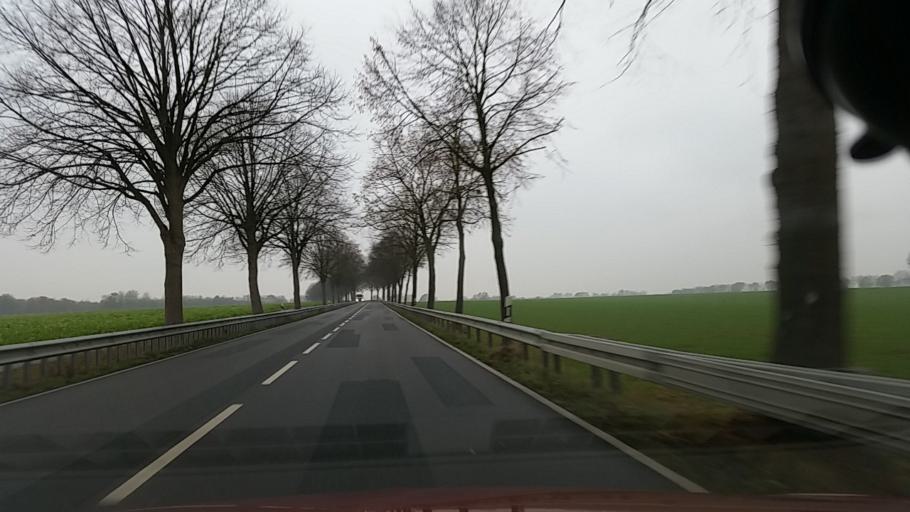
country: DE
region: Lower Saxony
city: Hankensbuttel
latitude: 52.7317
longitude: 10.6364
